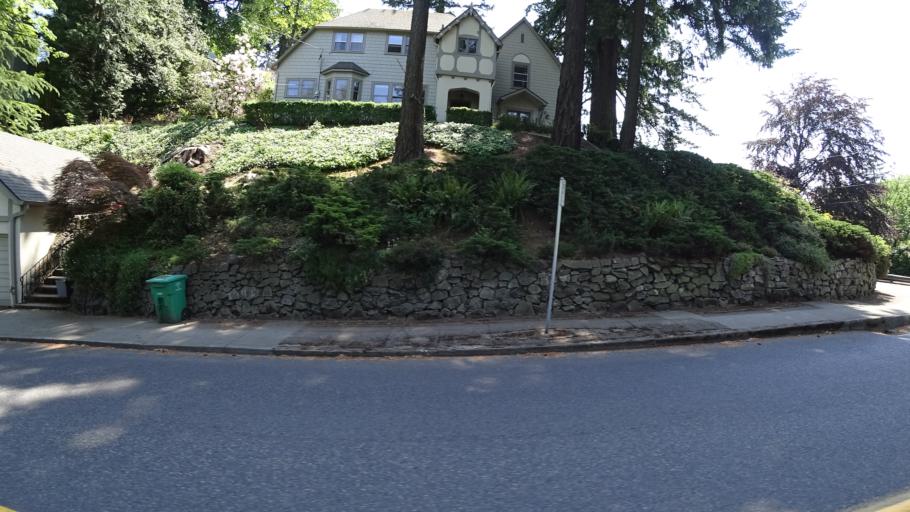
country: US
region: Oregon
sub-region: Multnomah County
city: Portland
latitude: 45.5081
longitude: -122.7040
